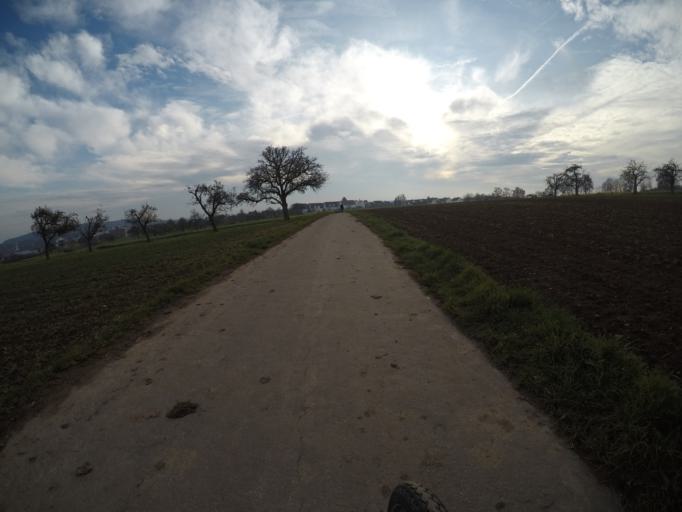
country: DE
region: Baden-Wuerttemberg
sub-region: Regierungsbezirk Stuttgart
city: Steinenbronn
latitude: 48.6997
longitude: 9.1209
